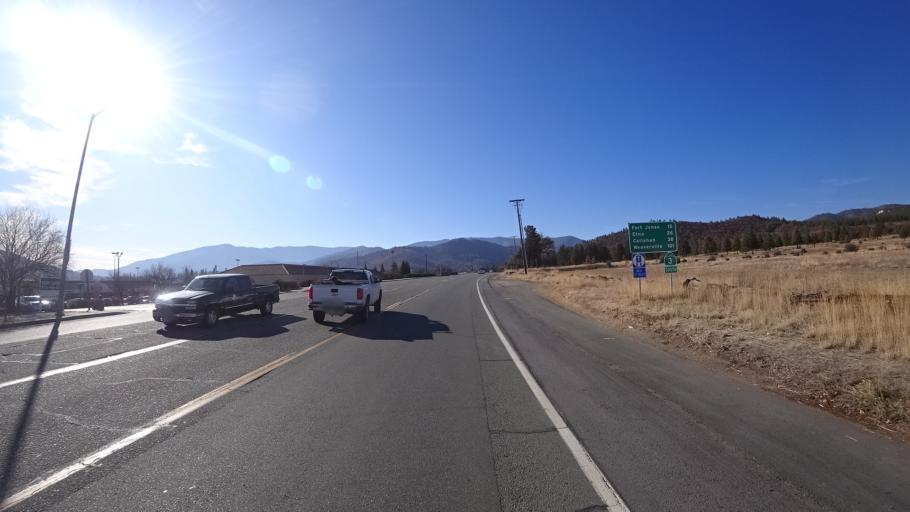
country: US
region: California
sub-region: Siskiyou County
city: Yreka
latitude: 41.7008
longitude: -122.6466
